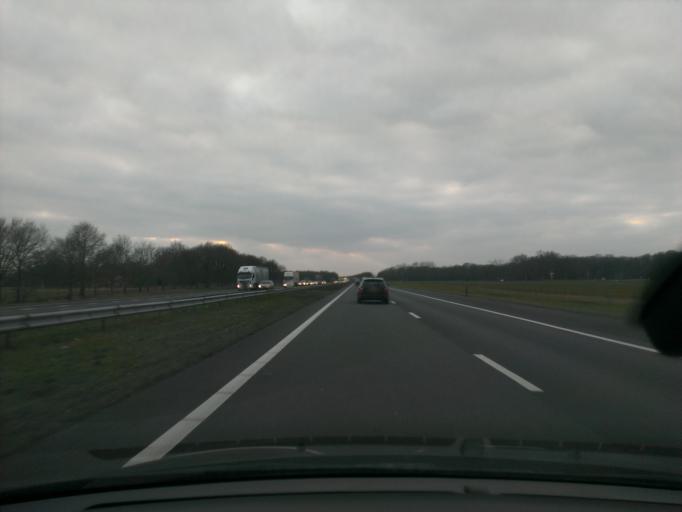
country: NL
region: Gelderland
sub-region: Gemeente Lochem
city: Harfsen
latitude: 52.2432
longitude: 6.3003
